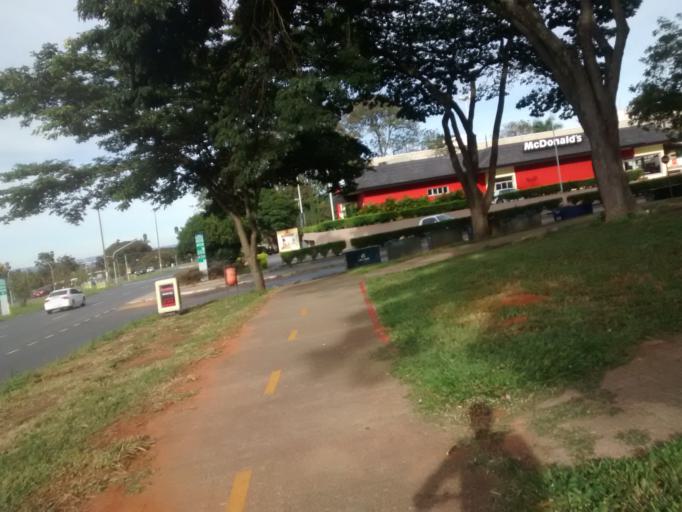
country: BR
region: Federal District
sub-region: Brasilia
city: Brasilia
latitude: -15.8147
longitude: -47.8885
